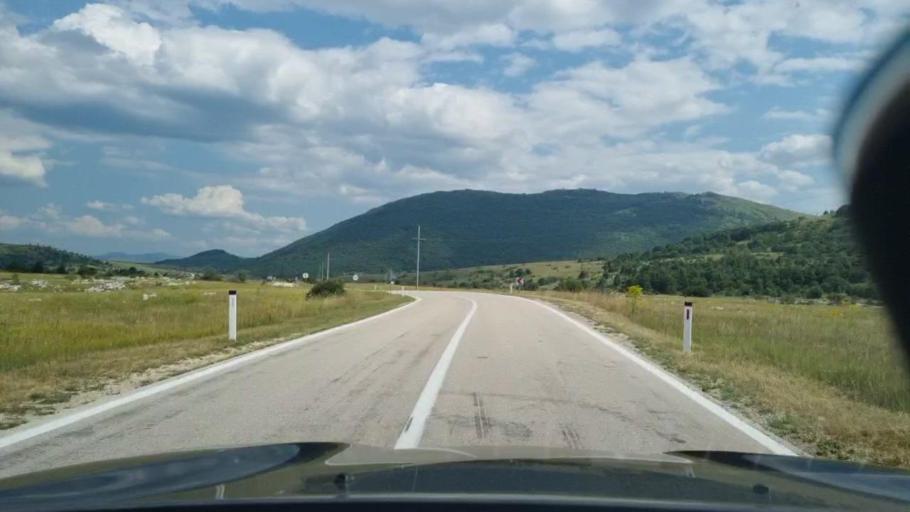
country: BA
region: Federation of Bosnia and Herzegovina
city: Bosansko Grahovo
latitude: 44.1438
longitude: 16.4637
